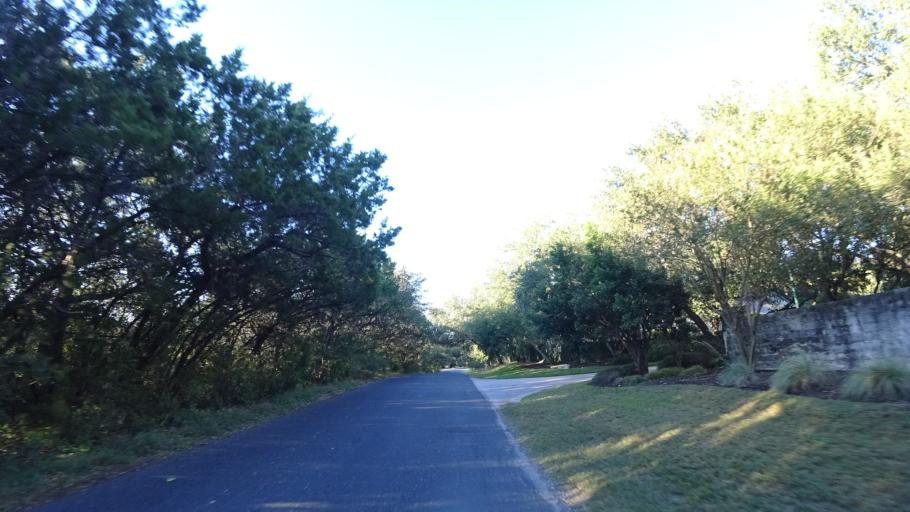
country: US
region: Texas
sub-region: Travis County
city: West Lake Hills
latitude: 30.3433
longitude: -97.8080
